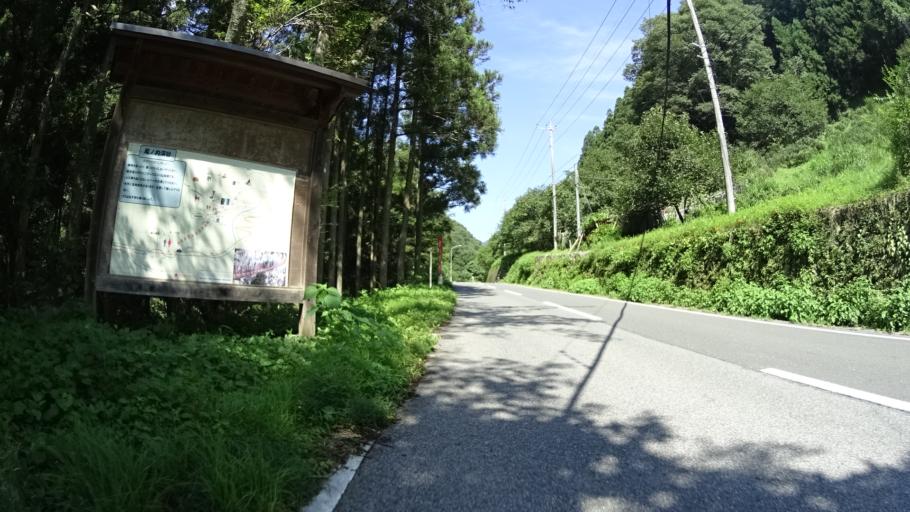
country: JP
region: Saitama
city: Chichibu
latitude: 36.0452
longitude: 138.8912
